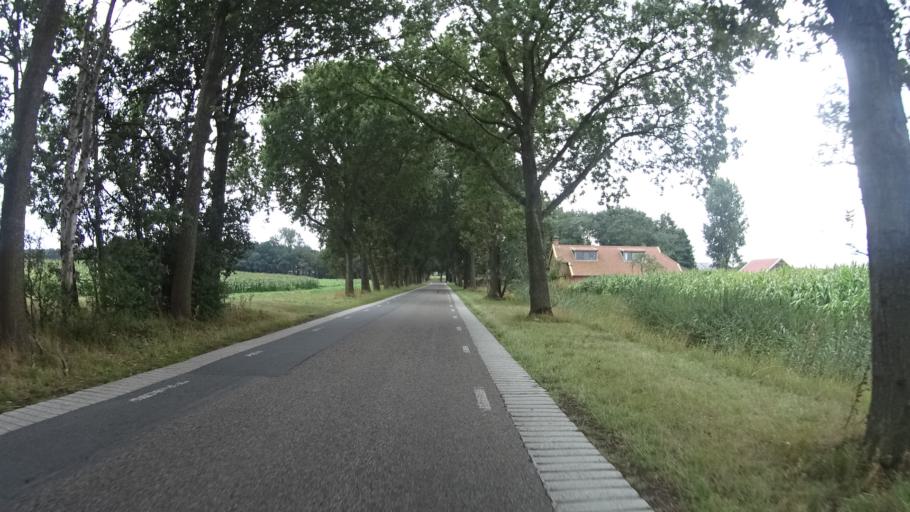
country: NL
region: Groningen
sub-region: Gemeente Slochteren
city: Slochteren
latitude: 53.1964
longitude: 6.8394
